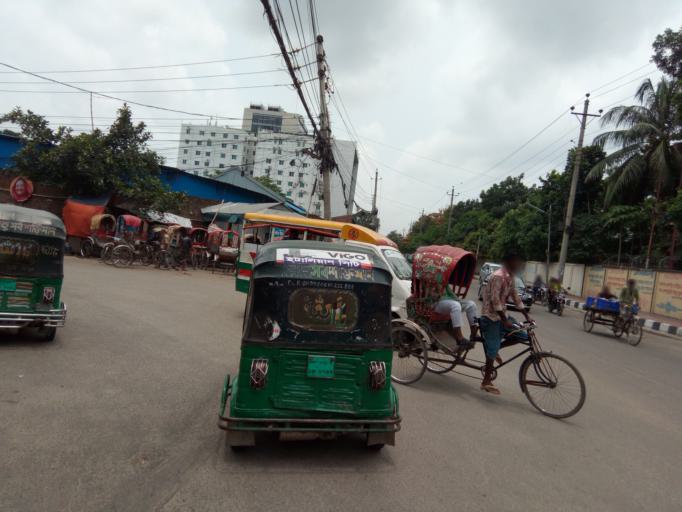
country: BD
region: Dhaka
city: Paltan
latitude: 23.7630
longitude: 90.4049
